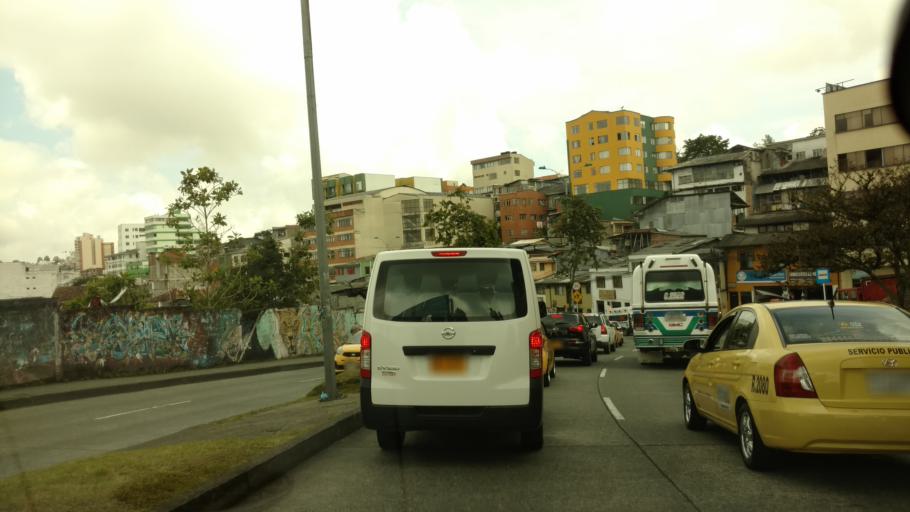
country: CO
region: Caldas
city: Manizales
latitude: 5.0645
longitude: -75.5037
